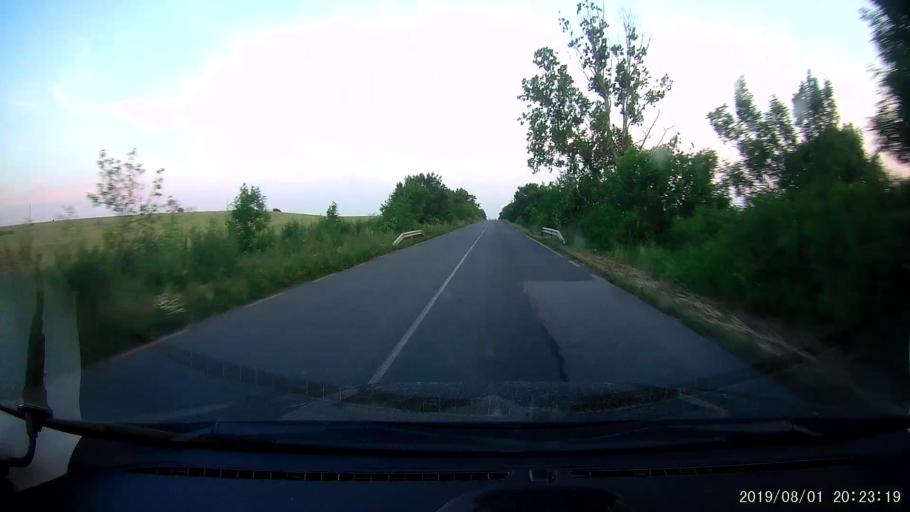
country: BG
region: Yambol
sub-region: Obshtina Elkhovo
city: Elkhovo
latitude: 42.2510
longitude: 26.5988
